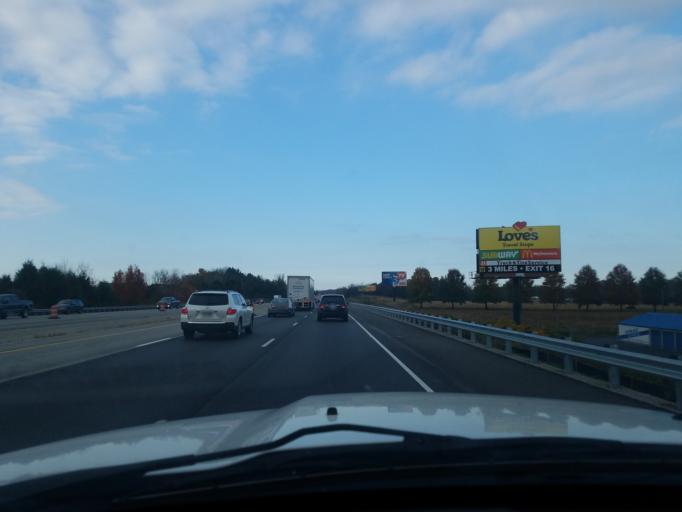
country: US
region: Indiana
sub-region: Clark County
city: Sellersburg
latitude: 38.4428
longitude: -85.7665
